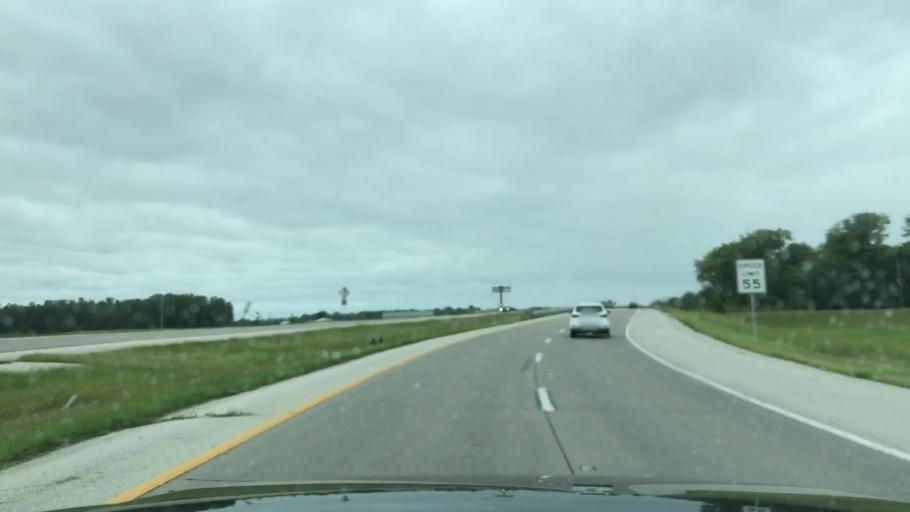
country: US
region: Missouri
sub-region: Saint Charles County
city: Saint Charles
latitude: 38.7288
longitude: -90.4944
